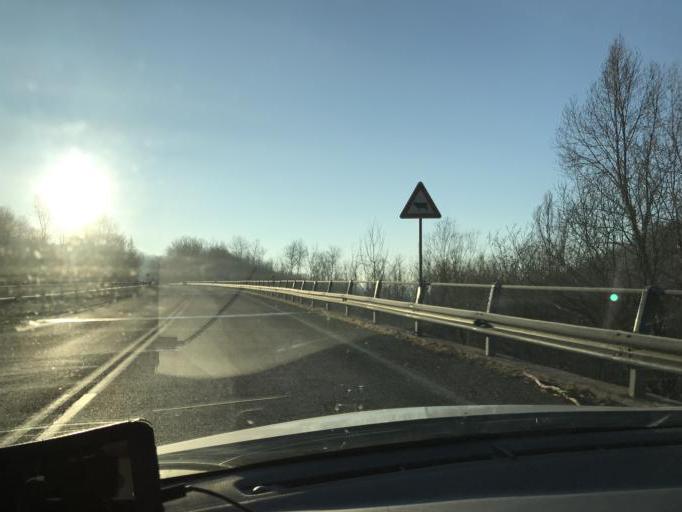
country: IT
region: Latium
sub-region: Provincia di Rieti
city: Petrella Salto
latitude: 42.3079
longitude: 13.0364
